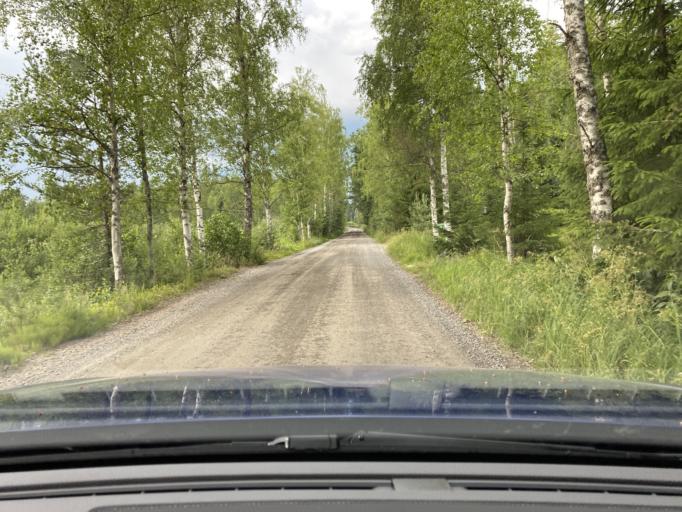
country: FI
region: Satakunta
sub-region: Rauma
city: Lappi
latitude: 61.1393
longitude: 21.9071
